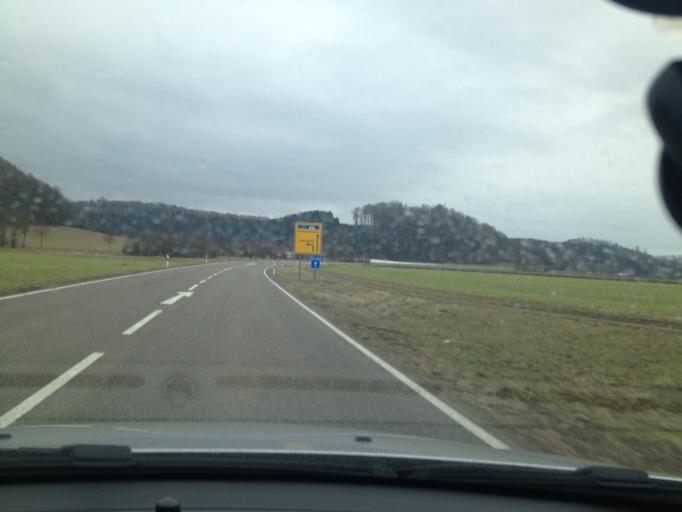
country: DE
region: Bavaria
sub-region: Swabia
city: Zusmarshausen
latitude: 48.4325
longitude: 10.5963
